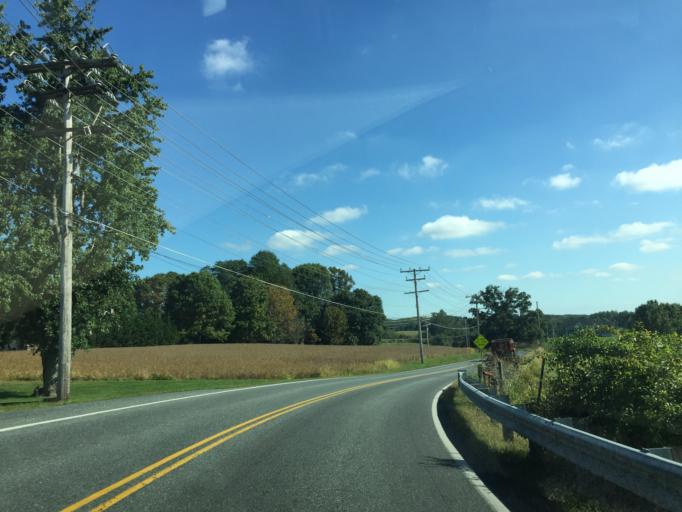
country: US
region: Maryland
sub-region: Harford County
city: Bel Air North
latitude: 39.5810
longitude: -76.4179
